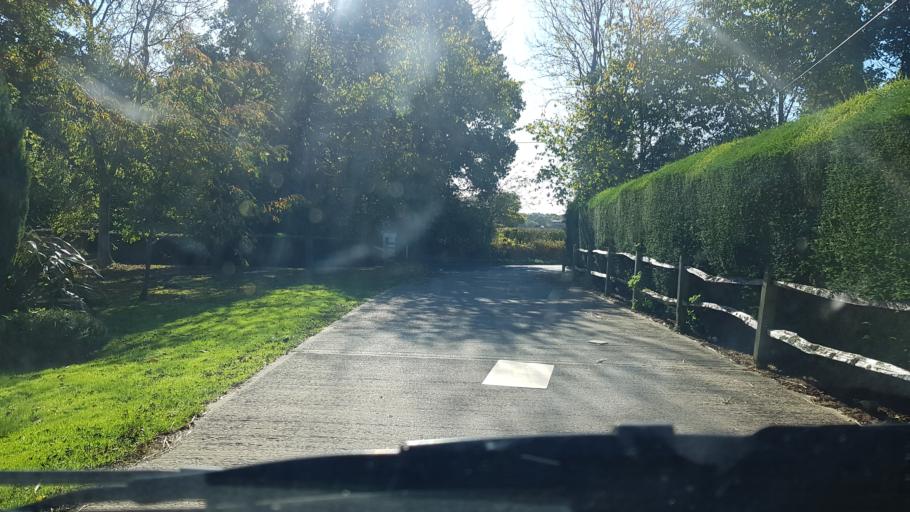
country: GB
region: England
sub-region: Surrey
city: Newdigate
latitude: 51.1169
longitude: -0.2884
